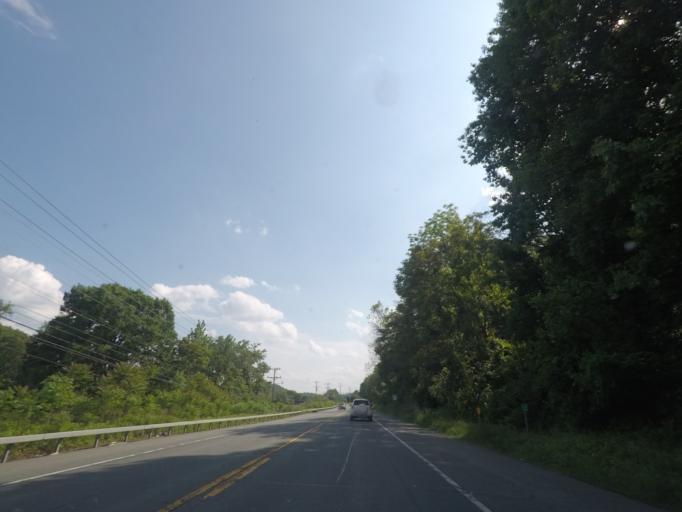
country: US
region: New York
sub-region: Ulster County
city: Marlboro
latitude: 41.5863
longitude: -73.9833
